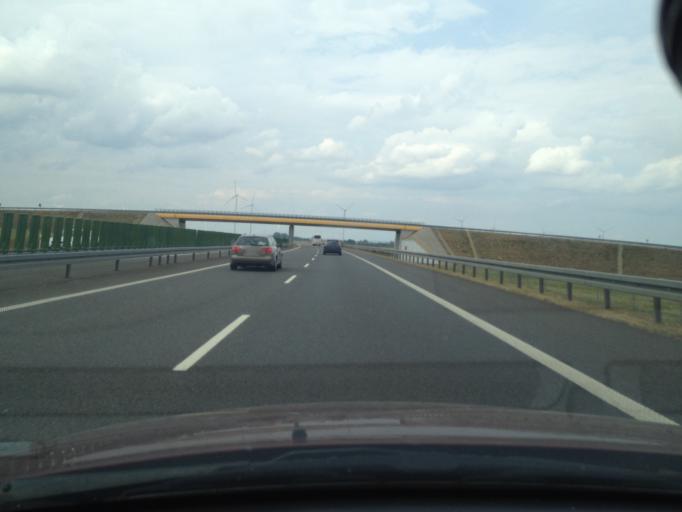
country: PL
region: West Pomeranian Voivodeship
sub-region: Powiat pyrzycki
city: Kozielice
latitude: 53.0786
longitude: 14.8557
